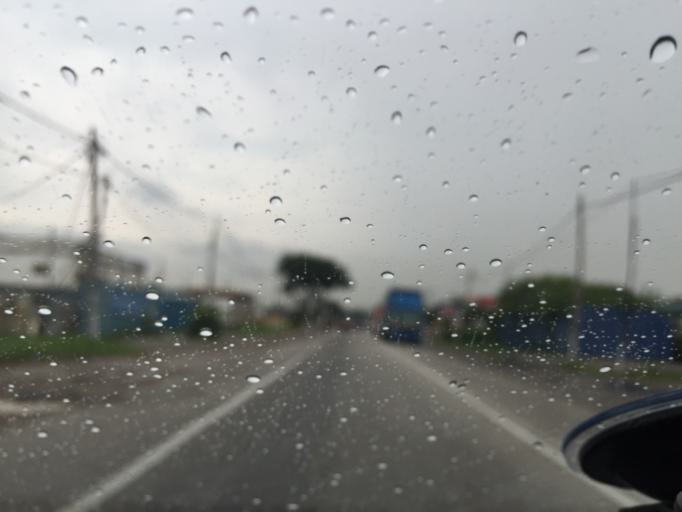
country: MY
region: Selangor
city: Subang Jaya
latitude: 3.0119
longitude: 101.5205
